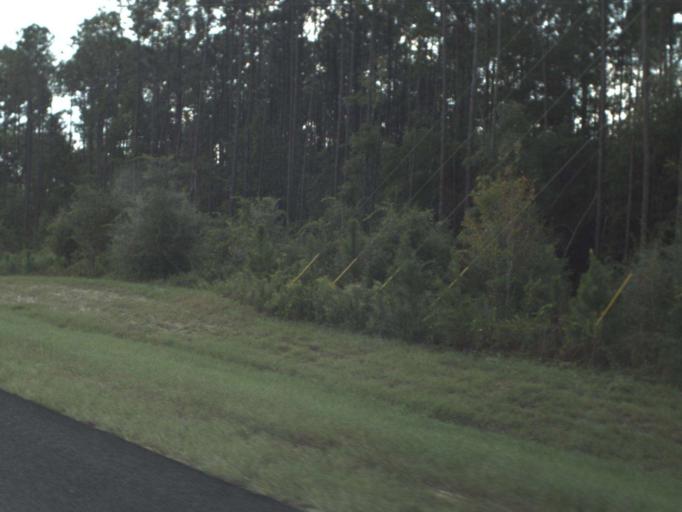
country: US
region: Florida
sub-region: Bay County
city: Laguna Beach
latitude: 30.4533
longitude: -85.8733
